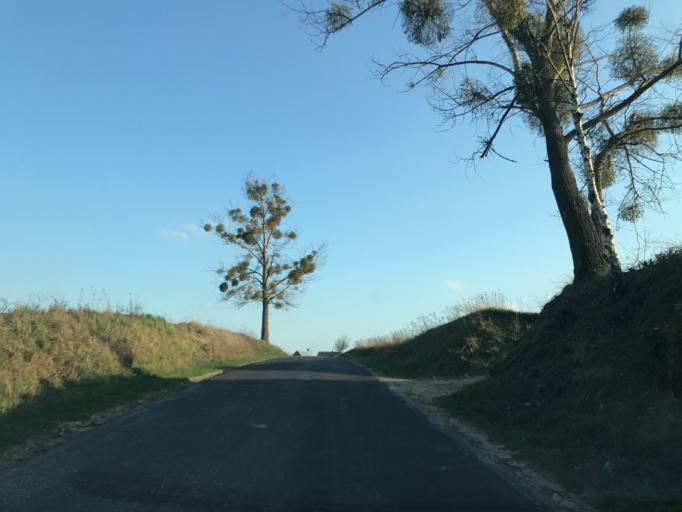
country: PL
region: Kujawsko-Pomorskie
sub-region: Powiat brodnicki
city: Bartniczka
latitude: 53.2387
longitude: 19.5998
